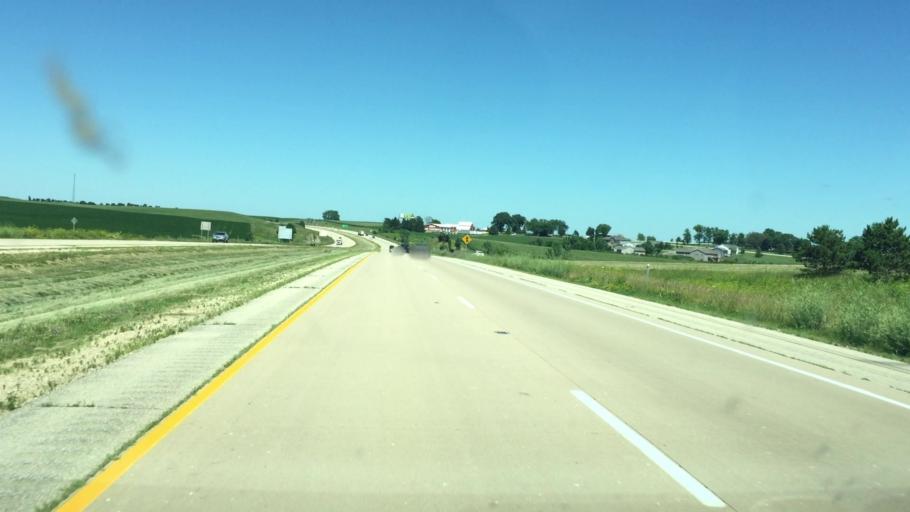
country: US
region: Wisconsin
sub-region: Grant County
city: Platteville
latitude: 42.7452
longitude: -90.3373
